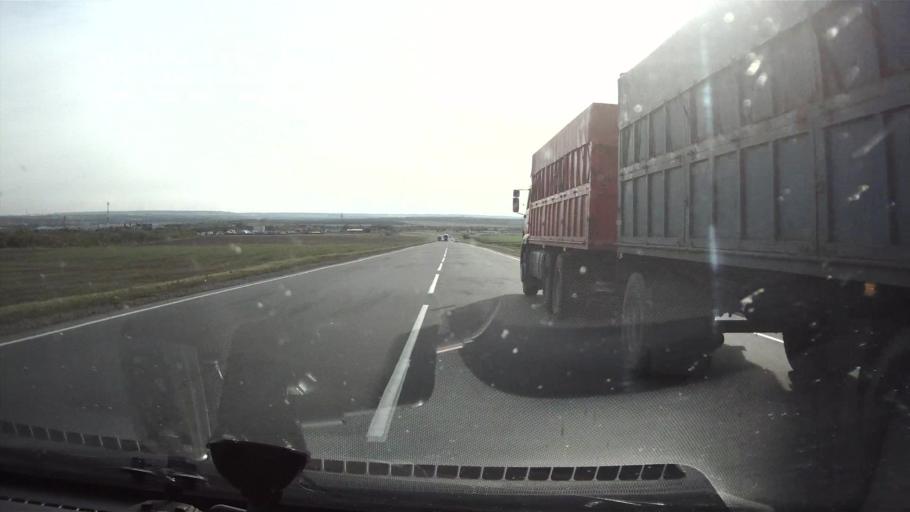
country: RU
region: Saratov
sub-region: Saratovskiy Rayon
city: Saratov
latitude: 51.7410
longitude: 46.0442
